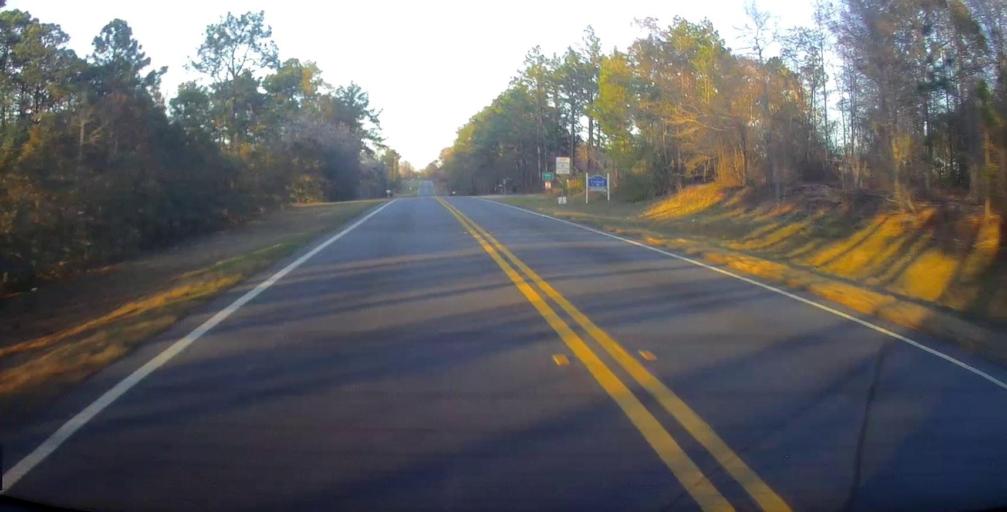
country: US
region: Georgia
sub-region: Dodge County
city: Chester
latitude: 32.3318
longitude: -83.0469
